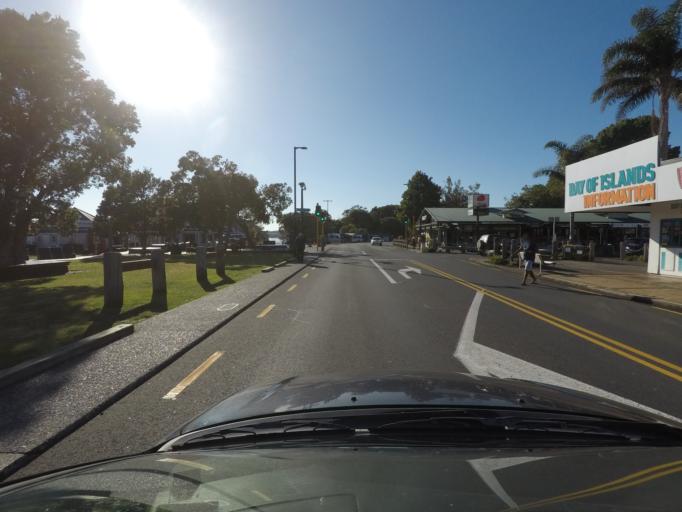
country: NZ
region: Northland
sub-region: Far North District
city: Paihia
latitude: -35.2812
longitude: 174.0918
